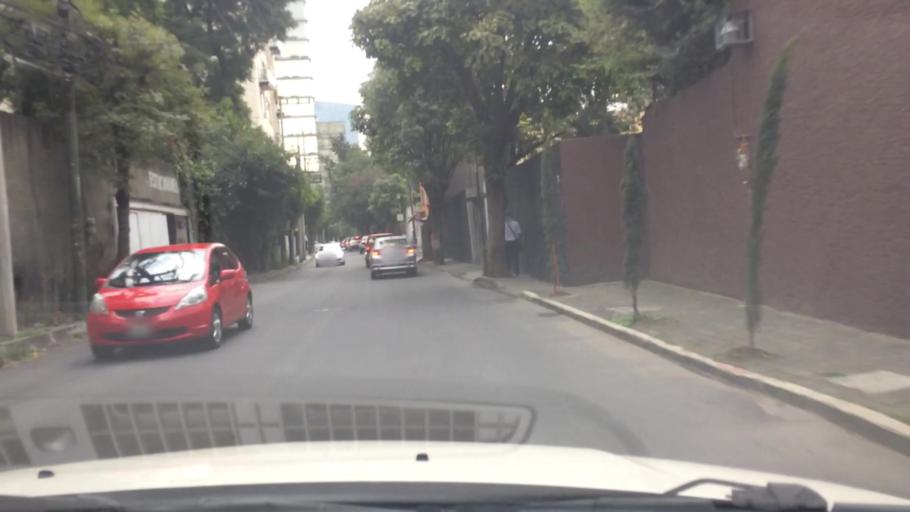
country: MX
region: Mexico City
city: Alvaro Obregon
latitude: 19.3570
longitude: -99.1957
